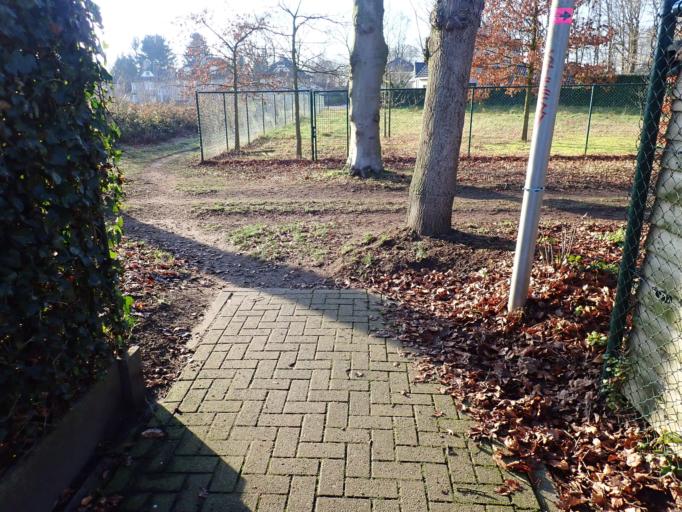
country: BE
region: Flanders
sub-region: Provincie Antwerpen
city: Essen
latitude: 51.4482
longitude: 4.4461
